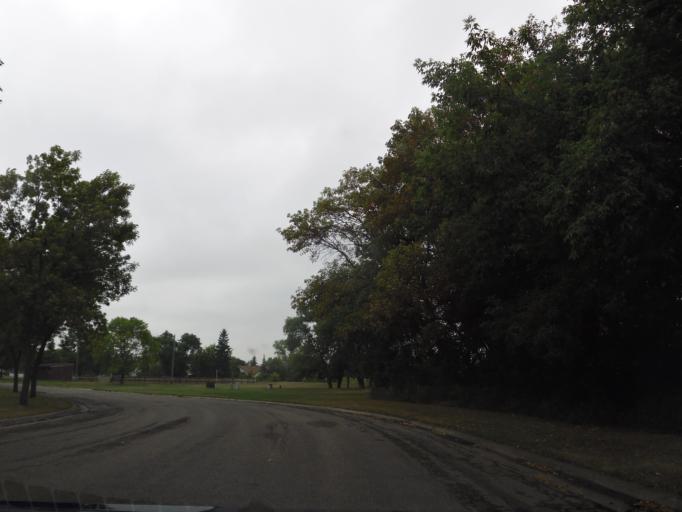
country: US
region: Minnesota
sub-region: Marshall County
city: Warren
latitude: 48.4476
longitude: -96.8744
